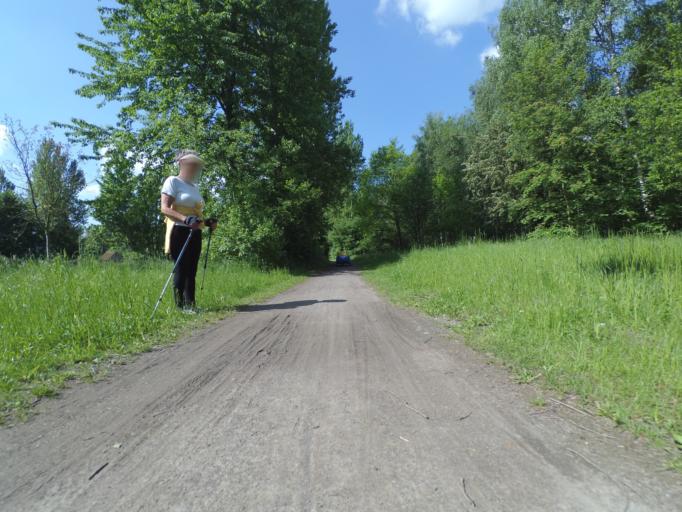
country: DE
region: Lower Saxony
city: Burgdorf
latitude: 52.4612
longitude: 10.0101
